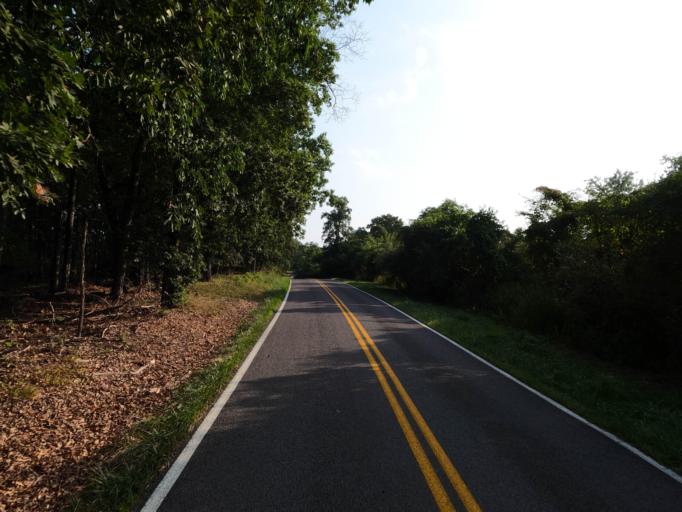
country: US
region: West Virginia
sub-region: Morgan County
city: Berkeley Springs
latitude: 39.6409
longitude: -78.2992
